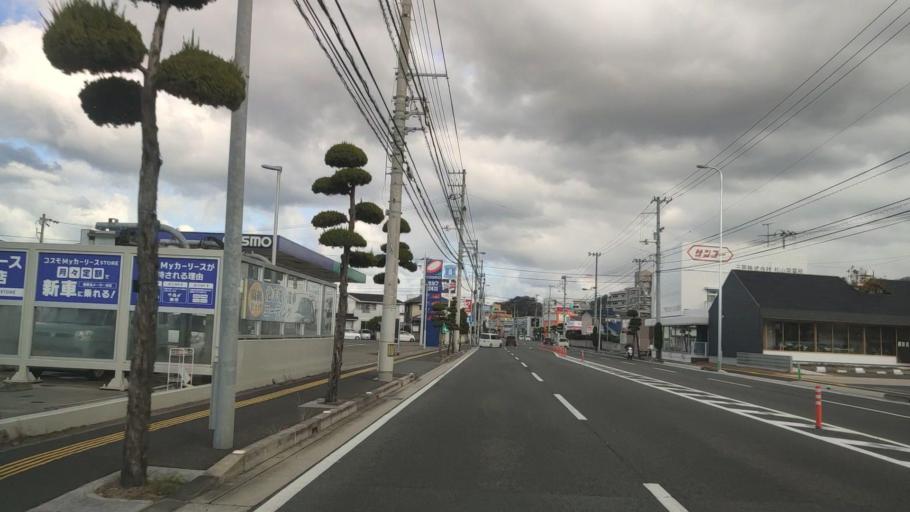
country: JP
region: Ehime
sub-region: Shikoku-chuo Shi
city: Matsuyama
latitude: 33.8678
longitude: 132.7515
